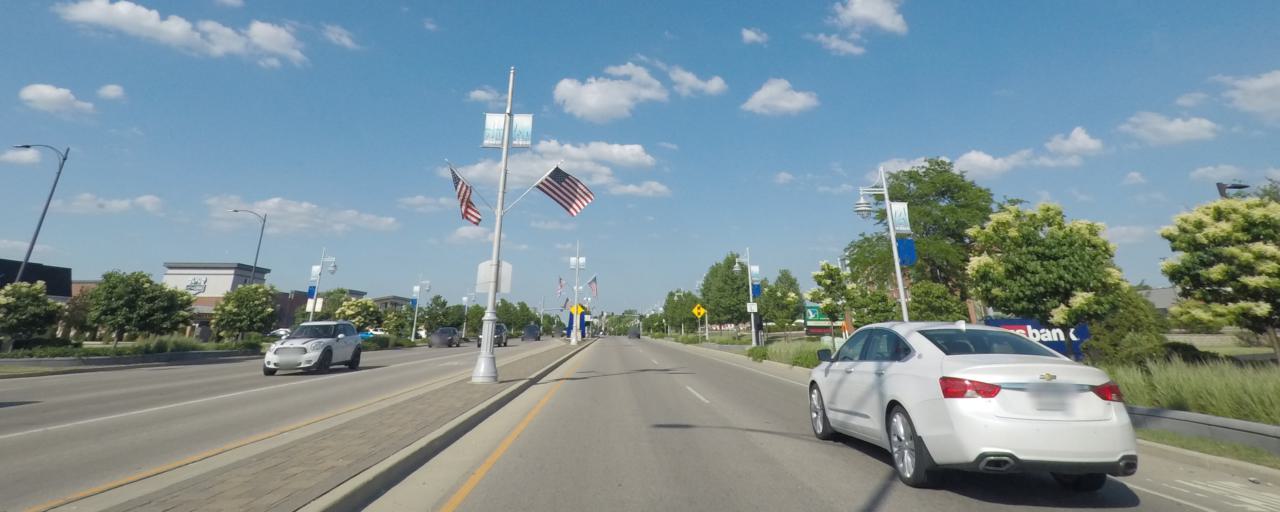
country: US
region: Wisconsin
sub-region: Waukesha County
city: Muskego
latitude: 42.9085
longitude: -88.1291
